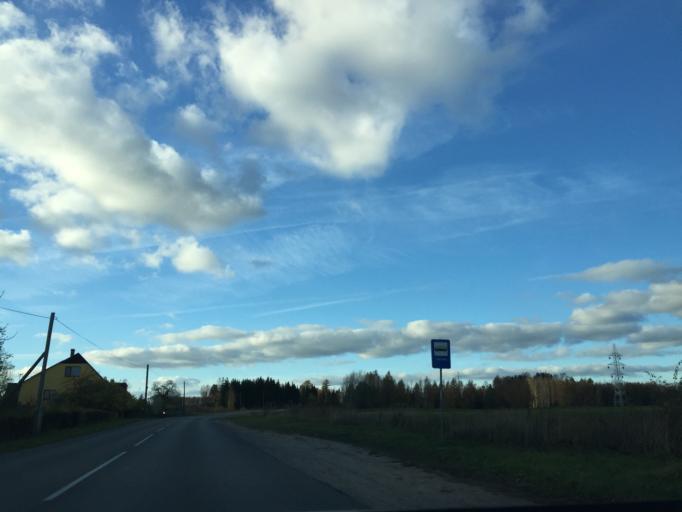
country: LV
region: Tukuma Rajons
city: Tukums
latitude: 56.9741
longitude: 23.1240
